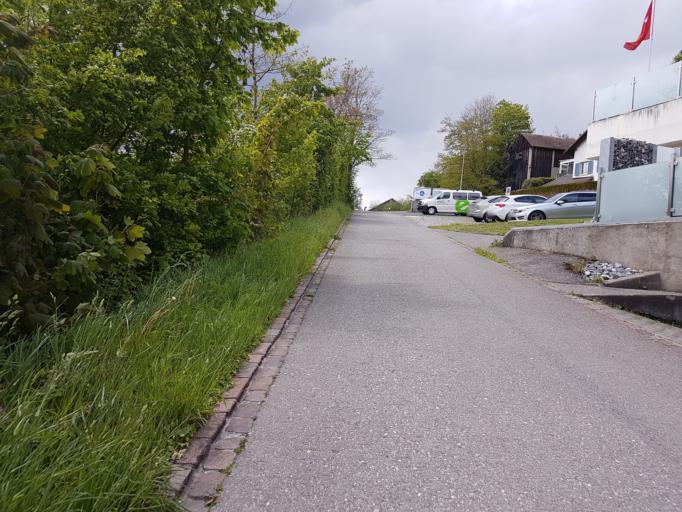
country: CH
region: Aargau
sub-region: Bezirk Brugg
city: Veltheim
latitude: 47.4155
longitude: 8.1527
